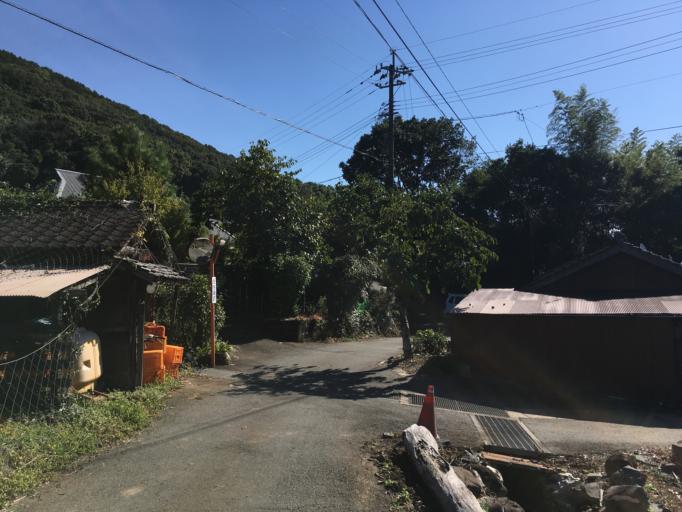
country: JP
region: Kumamoto
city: Kumamoto
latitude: 32.7987
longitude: 130.6569
